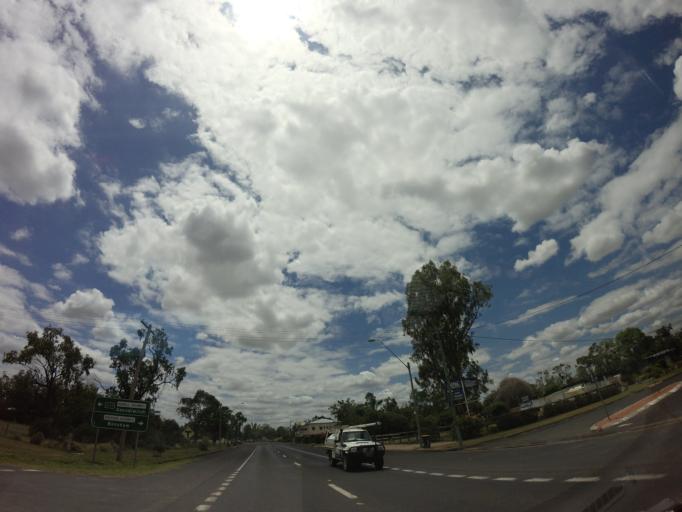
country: AU
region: New South Wales
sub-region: Moree Plains
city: Boggabilla
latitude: -28.6056
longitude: 150.3591
